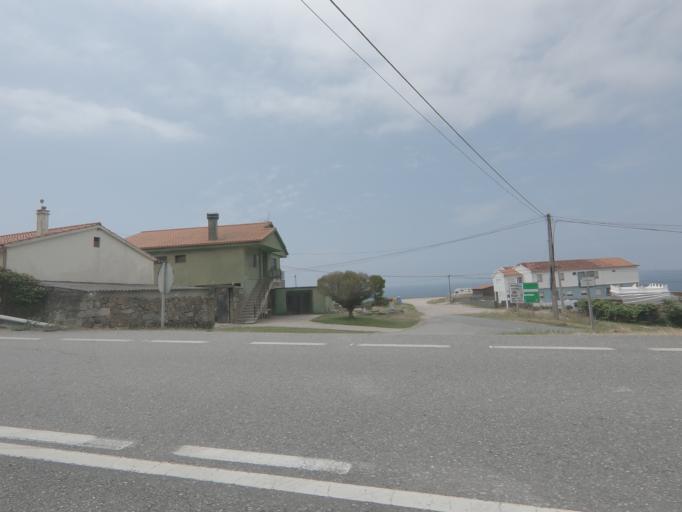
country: ES
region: Galicia
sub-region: Provincia de Pontevedra
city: O Rosal
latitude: 41.9500
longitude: -8.8832
